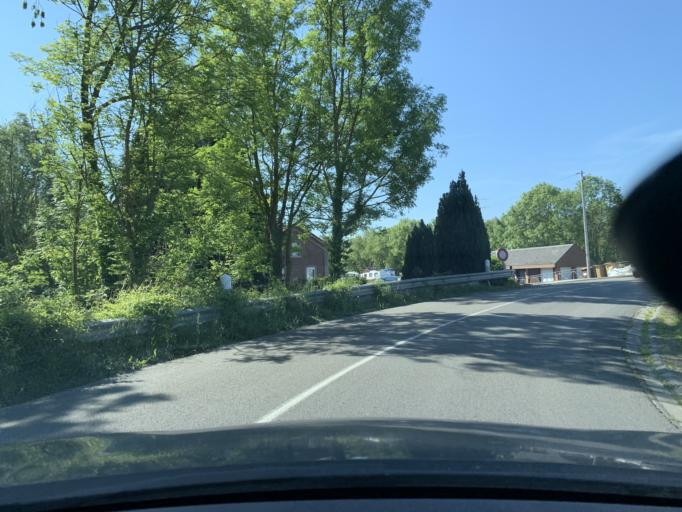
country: FR
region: Nord-Pas-de-Calais
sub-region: Departement du Nord
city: Rumilly-en-Cambresis
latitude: 50.1012
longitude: 3.2477
